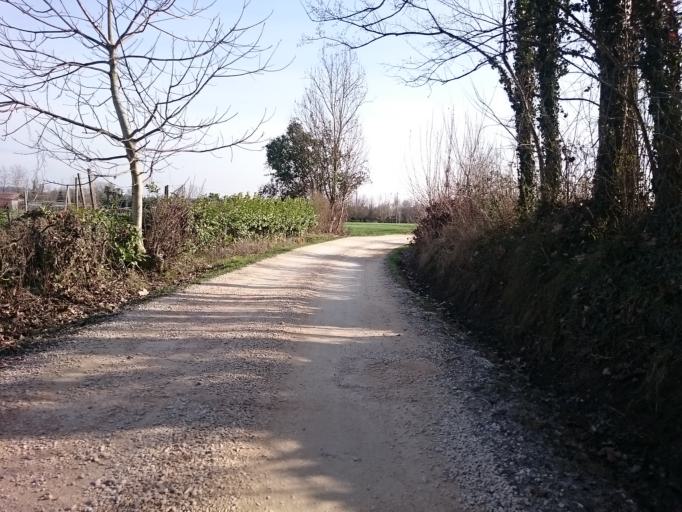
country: IT
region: Lombardy
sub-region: Provincia di Mantova
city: Ponti sul Mincio
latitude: 45.4209
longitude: 10.6980
